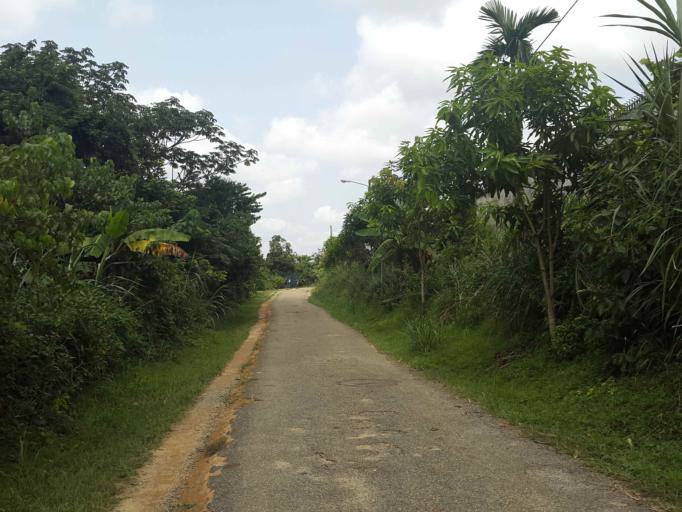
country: CM
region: Littoral
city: Douala
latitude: 4.0807
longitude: 9.7411
